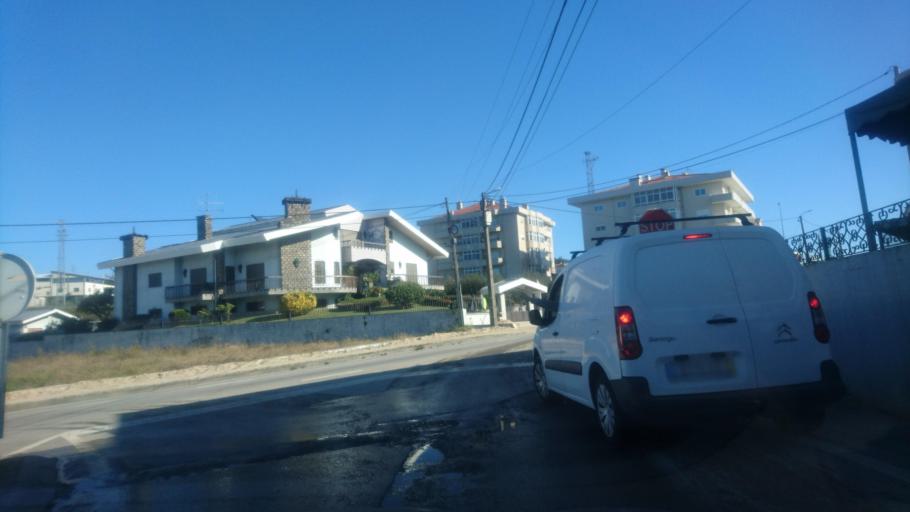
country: PT
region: Aveiro
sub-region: Oliveira de Azemeis
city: Sao Roque
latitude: 40.8858
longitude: -8.4569
